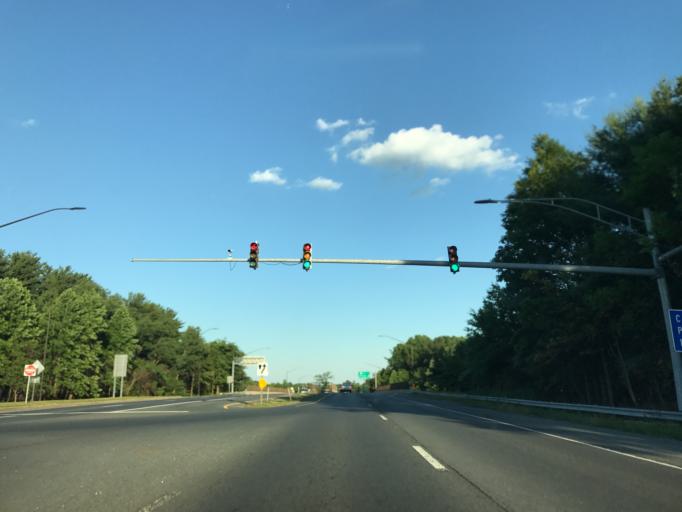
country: US
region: Maryland
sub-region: Anne Arundel County
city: Davidsonville
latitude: 38.9620
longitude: -76.6571
